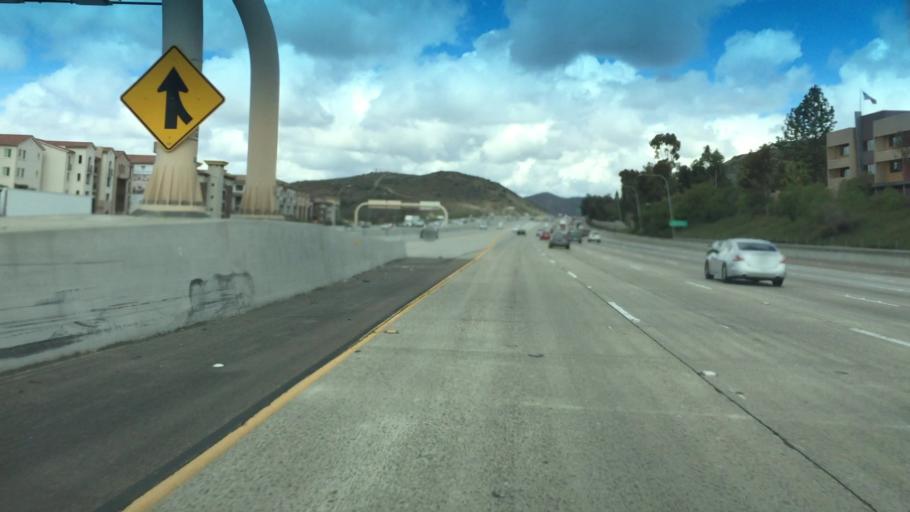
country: US
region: California
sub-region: San Diego County
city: Poway
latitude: 32.9187
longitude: -117.1157
